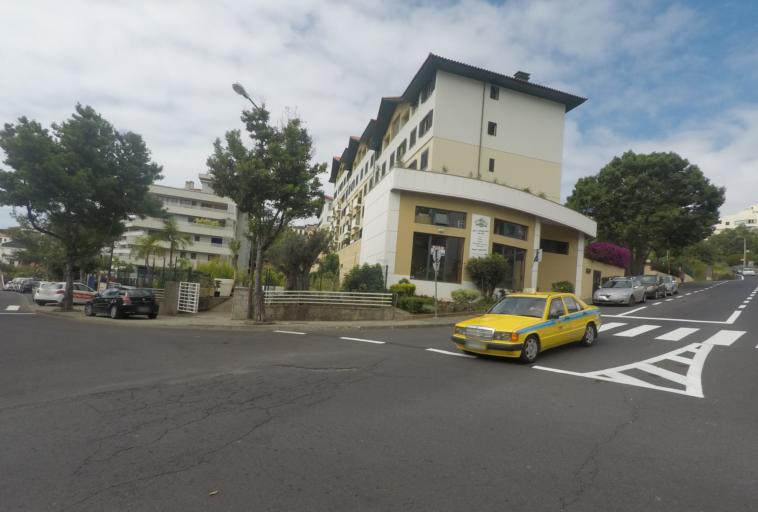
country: PT
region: Madeira
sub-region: Funchal
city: Funchal
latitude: 32.6474
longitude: -16.9301
